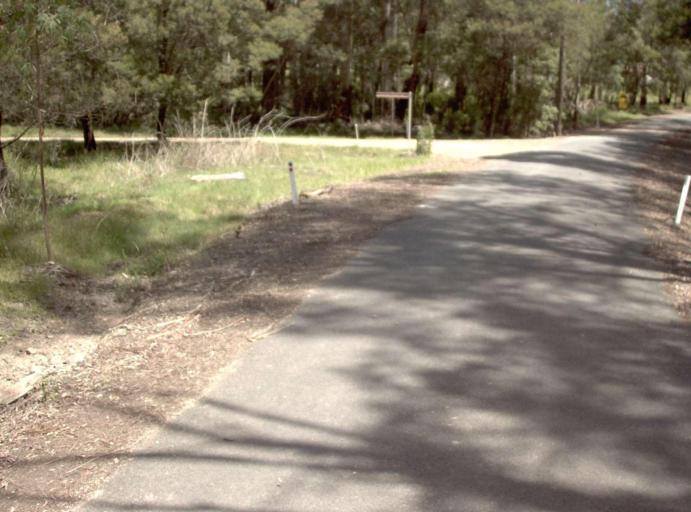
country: AU
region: New South Wales
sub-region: Bombala
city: Bombala
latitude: -37.4260
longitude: 149.0086
